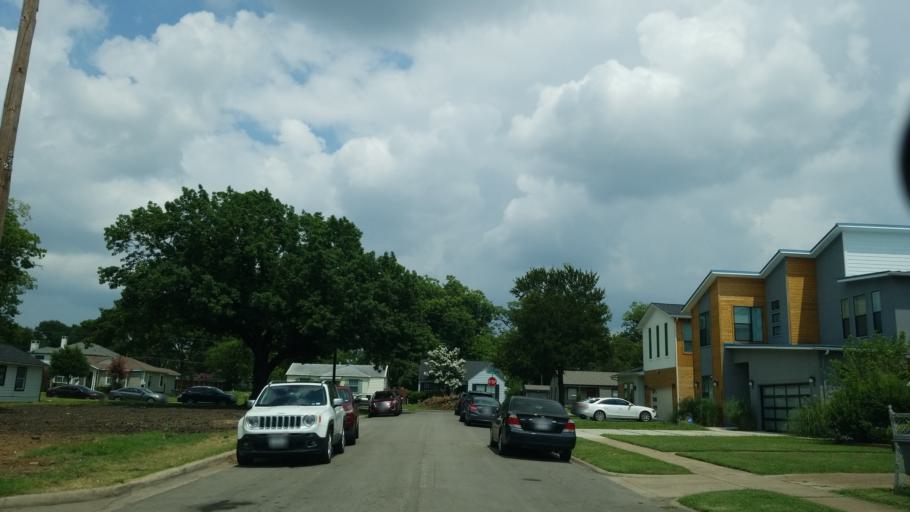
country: US
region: Texas
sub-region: Dallas County
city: University Park
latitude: 32.8477
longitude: -96.8281
